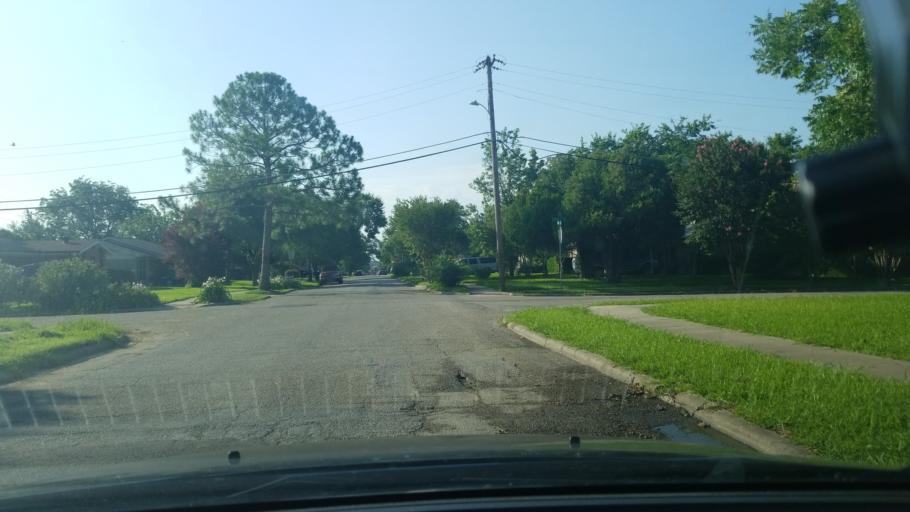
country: US
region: Texas
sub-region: Dallas County
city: Mesquite
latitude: 32.8141
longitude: -96.6388
